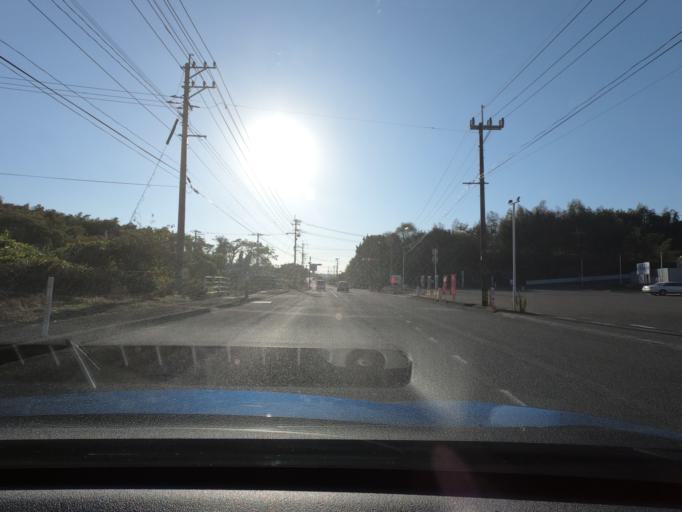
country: JP
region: Kagoshima
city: Akune
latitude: 32.0734
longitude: 130.2484
